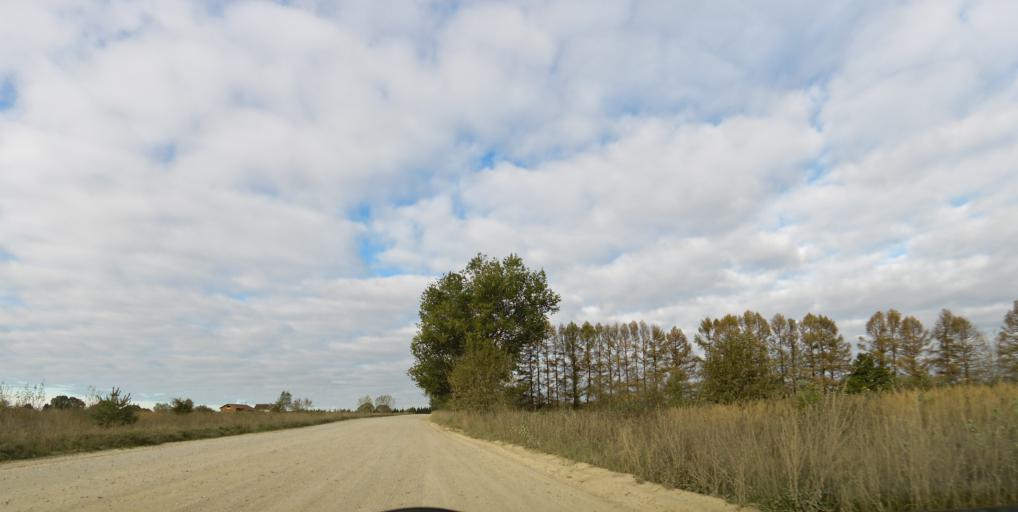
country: LT
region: Vilnius County
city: Pilaite
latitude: 54.7320
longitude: 25.1606
